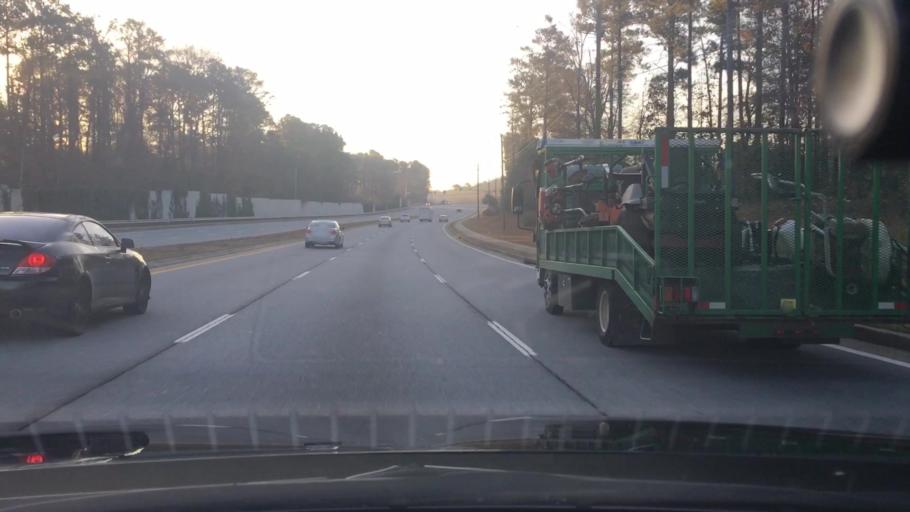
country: US
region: Georgia
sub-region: Fayette County
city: Peachtree City
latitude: 33.3859
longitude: -84.5796
